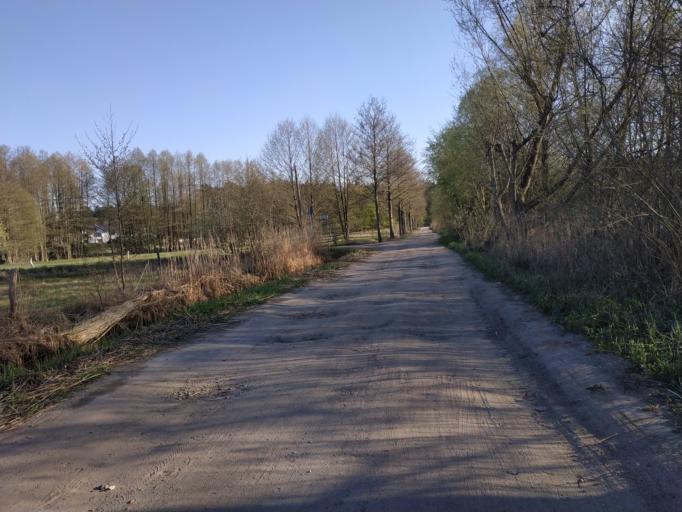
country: DE
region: Brandenburg
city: Strausberg
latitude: 52.5542
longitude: 13.8443
